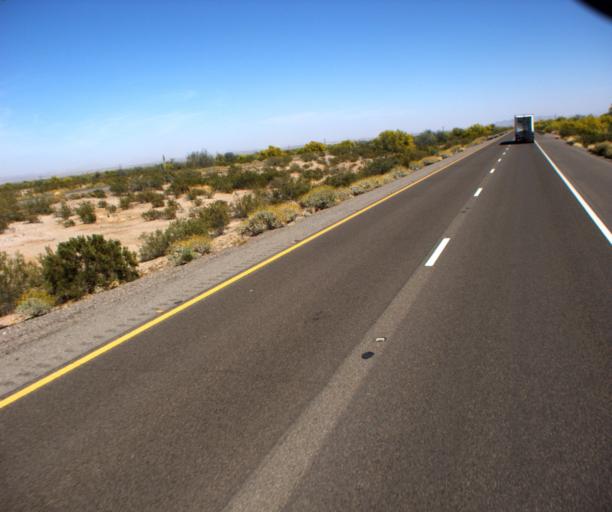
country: US
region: Arizona
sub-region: Pinal County
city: Maricopa
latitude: 32.8295
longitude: -112.0119
